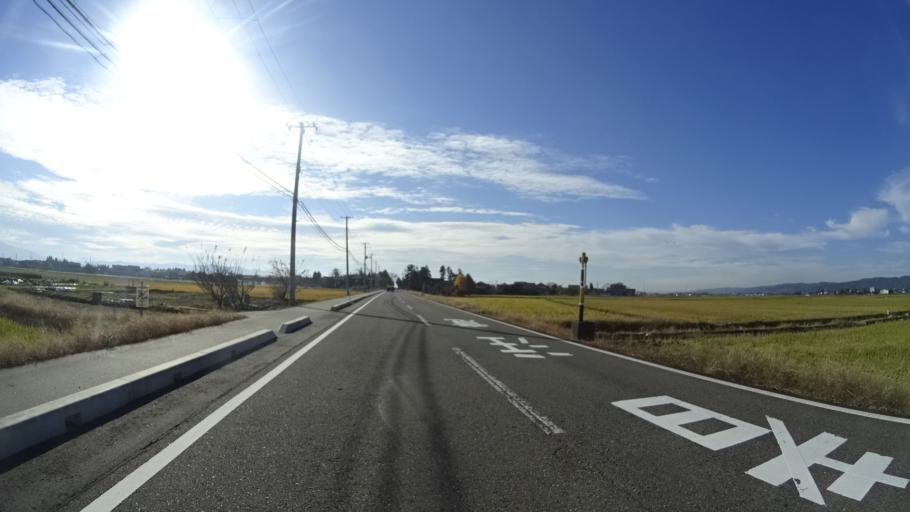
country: JP
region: Niigata
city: Mitsuke
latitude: 37.5609
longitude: 138.8493
